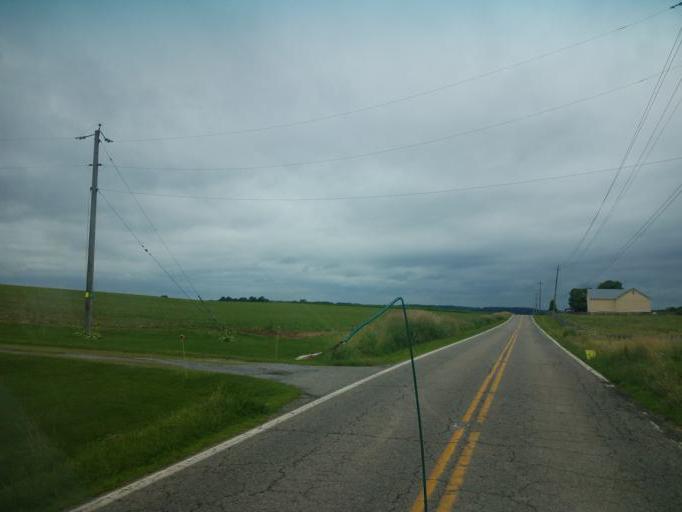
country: US
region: Ohio
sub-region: Columbiana County
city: Columbiana
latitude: 40.8297
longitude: -80.6915
